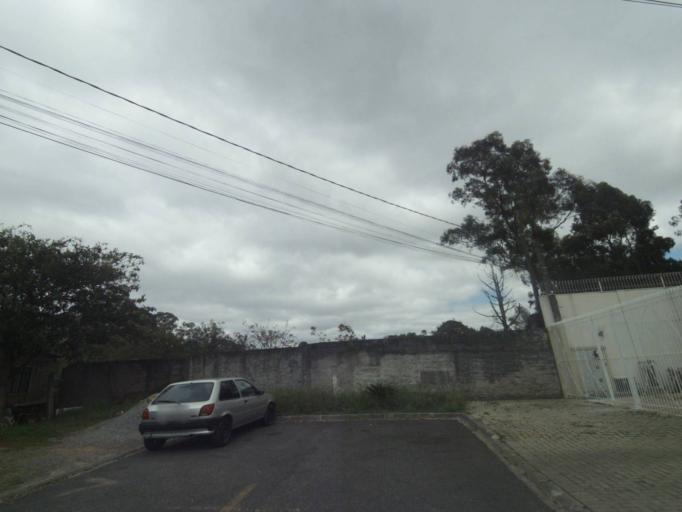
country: BR
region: Parana
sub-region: Pinhais
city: Pinhais
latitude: -25.4046
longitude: -49.2246
